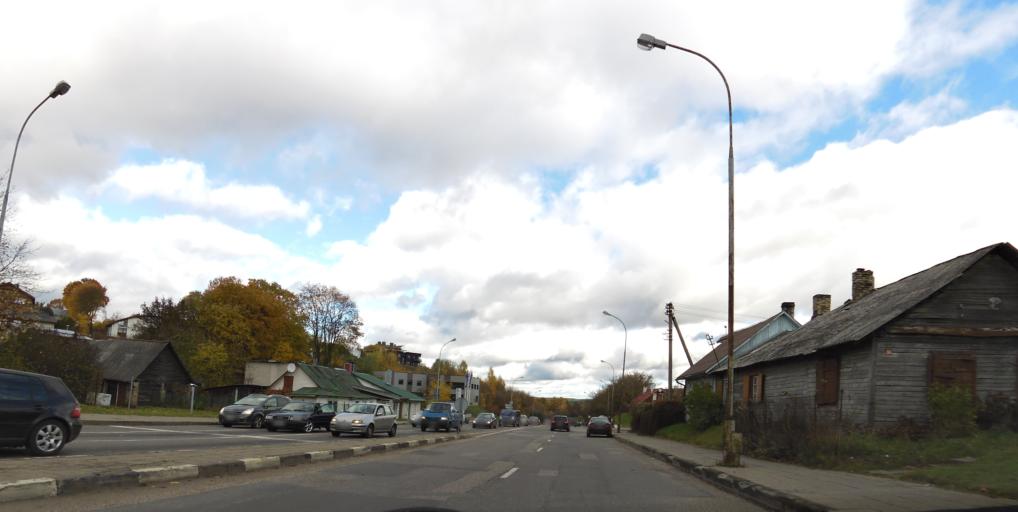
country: LT
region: Vilnius County
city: Rasos
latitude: 54.6622
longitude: 25.3016
